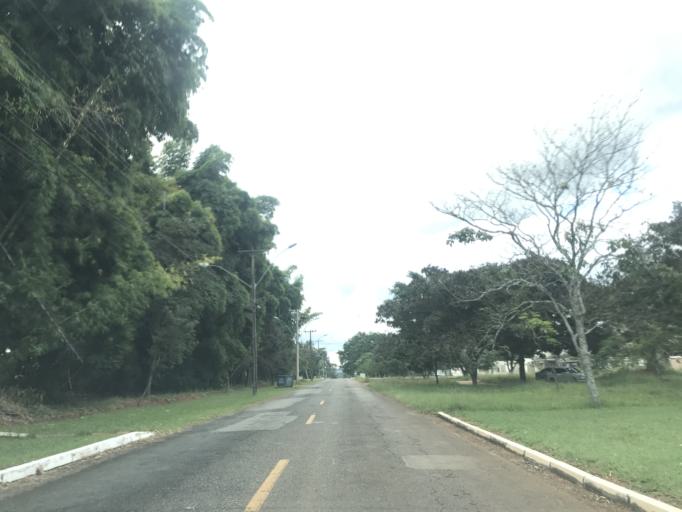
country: BR
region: Federal District
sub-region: Brasilia
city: Brasilia
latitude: -15.9074
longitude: -47.9404
